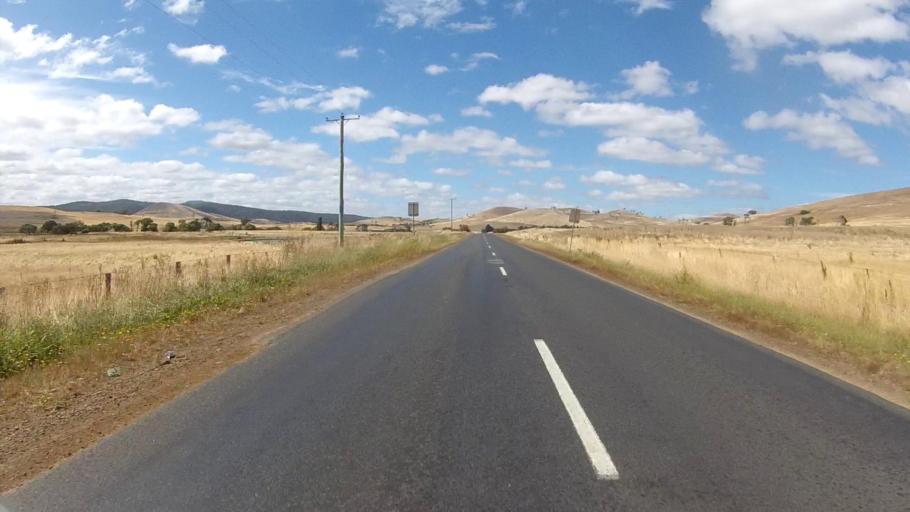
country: AU
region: Tasmania
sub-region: Brighton
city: Bridgewater
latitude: -42.5394
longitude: 147.3686
